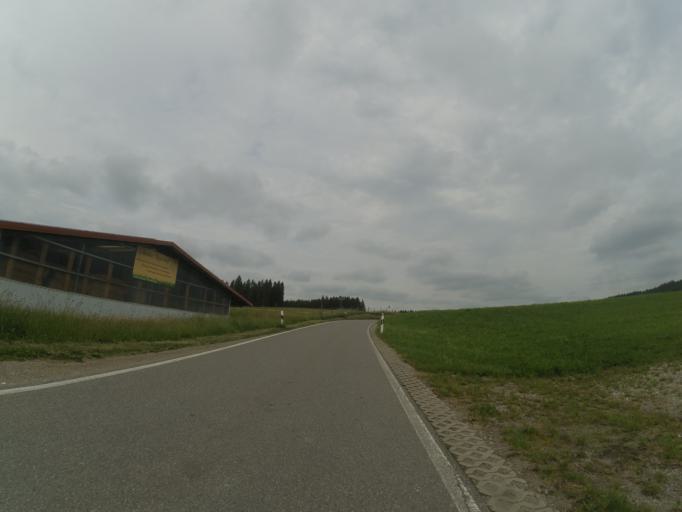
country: DE
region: Baden-Wuerttemberg
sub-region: Tuebingen Region
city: Isny im Allgau
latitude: 47.7282
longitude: 10.0453
